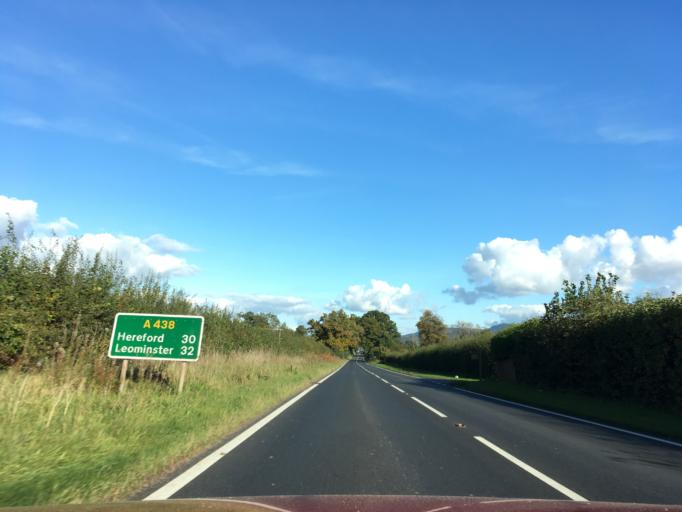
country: GB
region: Wales
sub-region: Sir Powys
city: Brecon
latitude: 52.0001
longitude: -3.2767
